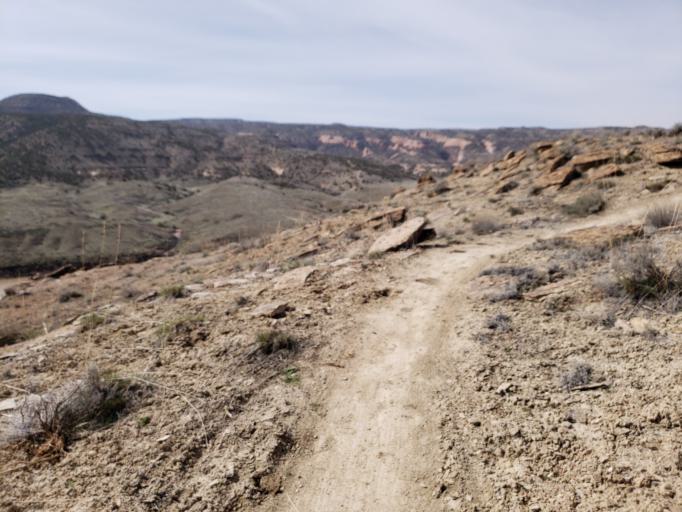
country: US
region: Colorado
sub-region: Mesa County
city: Loma
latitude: 39.1921
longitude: -108.8846
